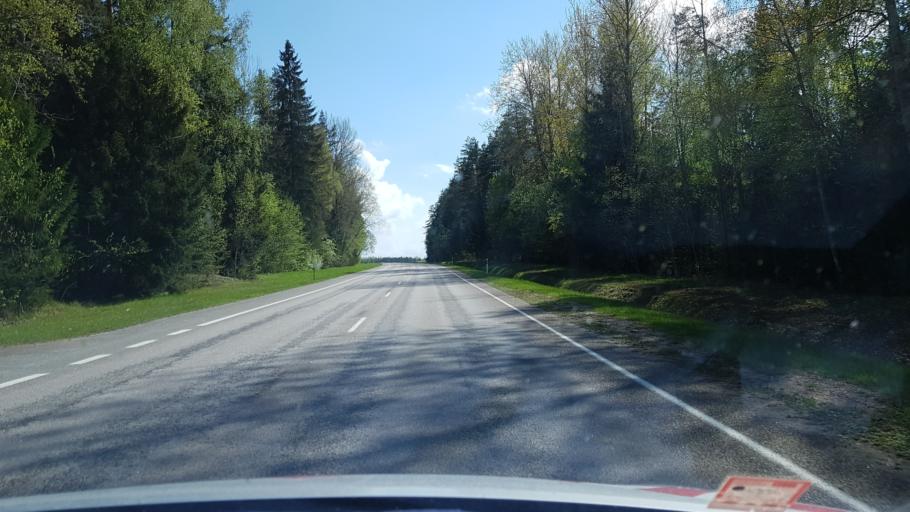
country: EE
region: Valgamaa
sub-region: Valga linn
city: Valga
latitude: 57.8465
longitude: 26.0584
